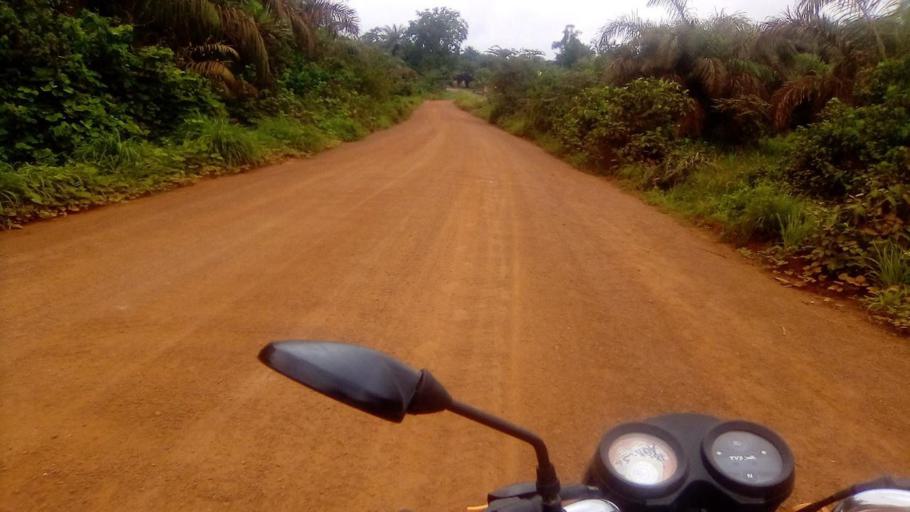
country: SL
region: Southern Province
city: Tongole
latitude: 7.4375
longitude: -11.8625
